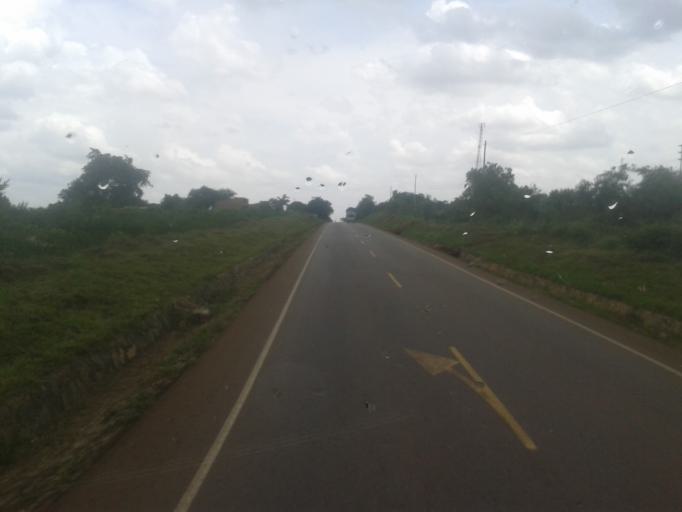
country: UG
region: Central Region
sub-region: Nakasongola District
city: Nakasongola
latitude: 1.3539
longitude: 32.3779
